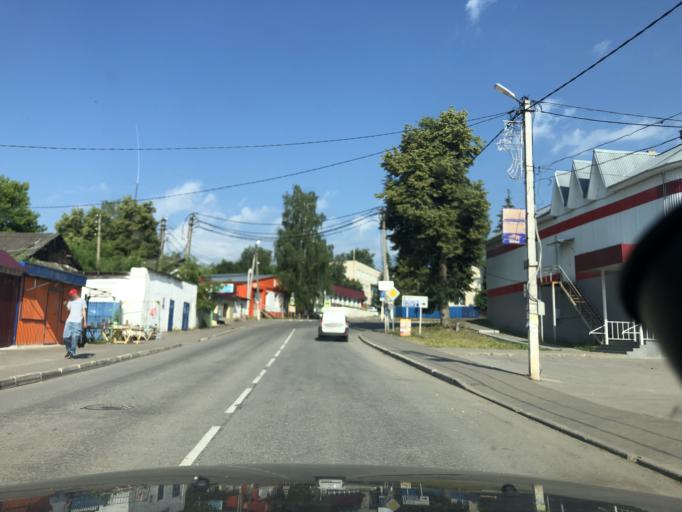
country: RU
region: Tula
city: Dubna
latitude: 54.1510
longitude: 36.9642
